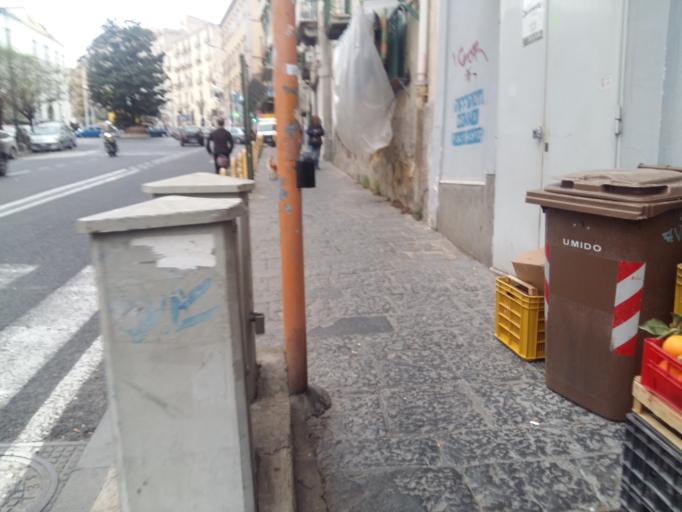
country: IT
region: Campania
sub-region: Provincia di Napoli
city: Napoli
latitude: 40.8519
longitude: 14.2398
